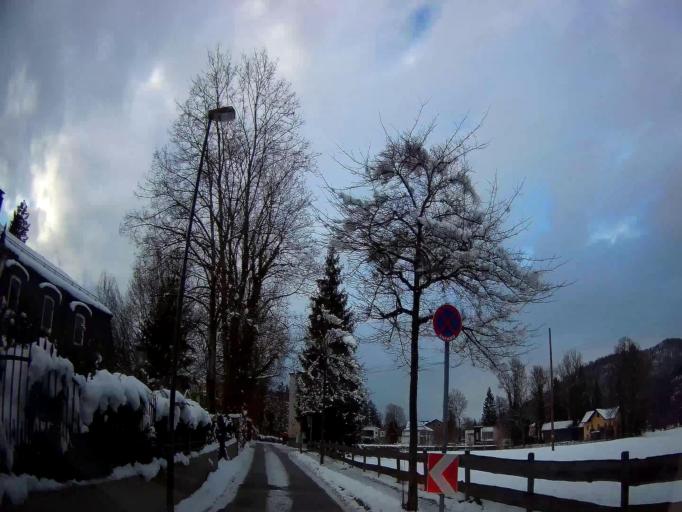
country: AT
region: Salzburg
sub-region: Salzburg Stadt
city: Salzburg
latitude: 47.7936
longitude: 13.0814
